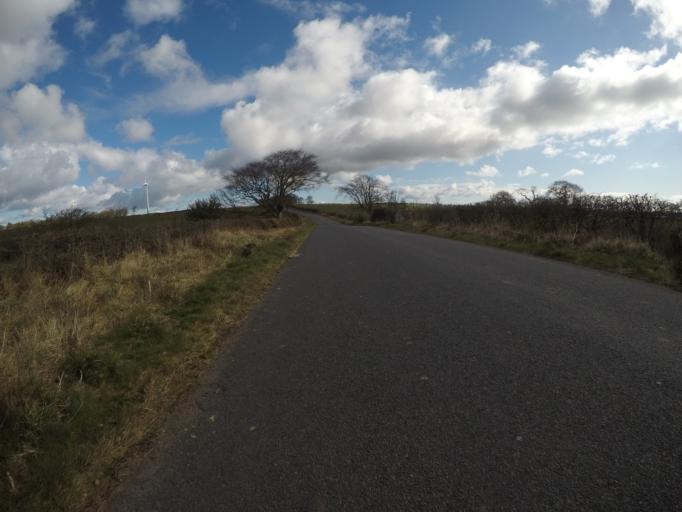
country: GB
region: Scotland
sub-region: North Ayrshire
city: Kilwinning
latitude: 55.6763
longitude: -4.6570
